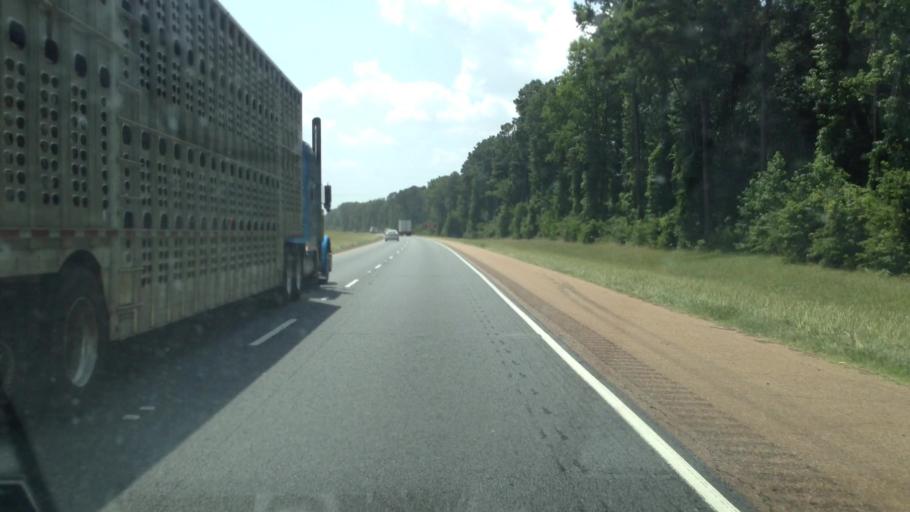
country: US
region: Louisiana
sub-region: Bienville Parish
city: Arcadia
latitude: 32.5667
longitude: -92.9252
